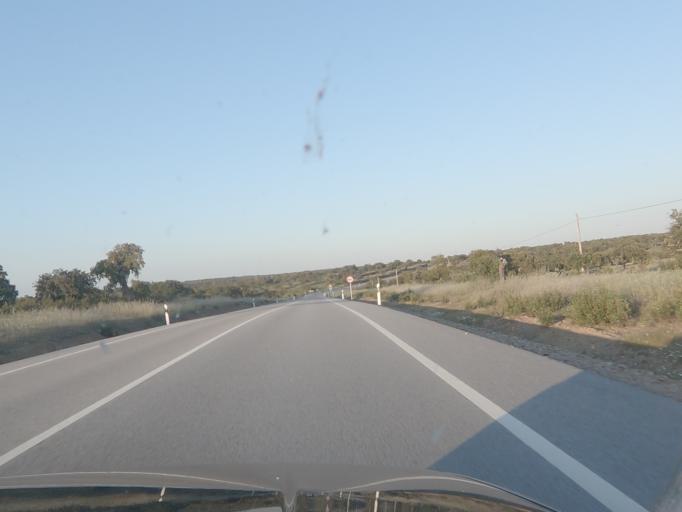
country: ES
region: Extremadura
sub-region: Provincia de Caceres
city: Carbajo
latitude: 39.5038
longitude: -7.1650
